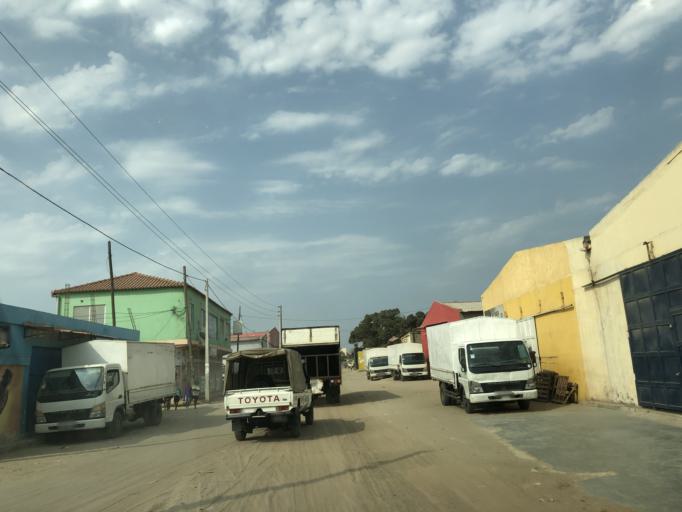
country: AO
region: Luanda
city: Luanda
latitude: -8.8945
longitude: 13.3528
